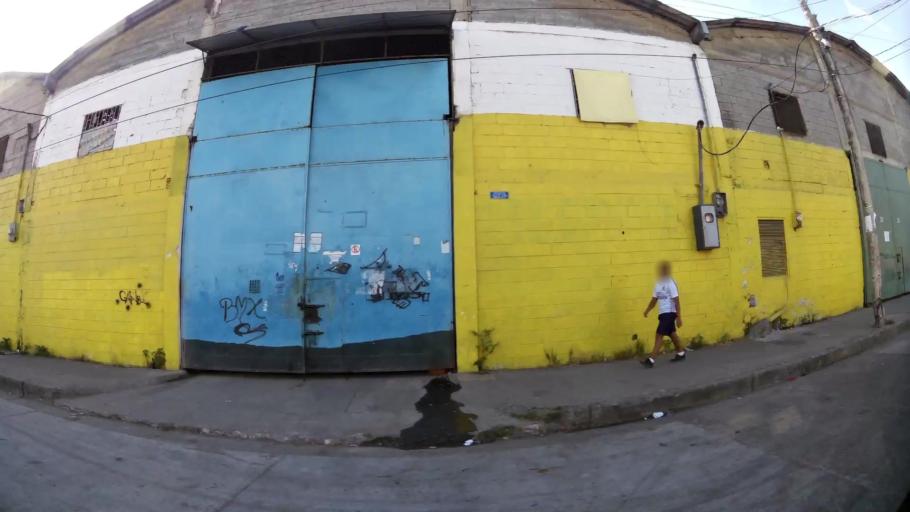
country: EC
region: Guayas
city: Guayaquil
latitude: -2.1553
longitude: -79.9263
